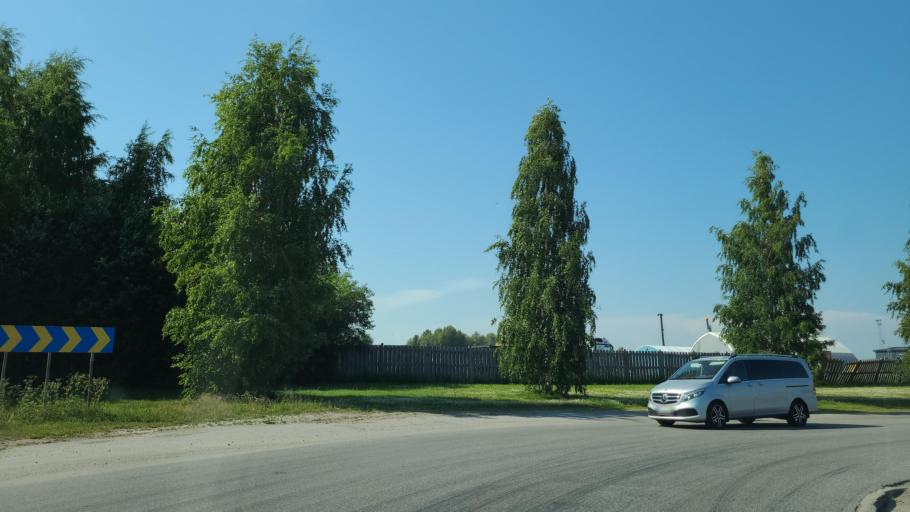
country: SE
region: Vaesterbotten
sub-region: Umea Kommun
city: Roback
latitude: 63.8449
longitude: 20.2114
